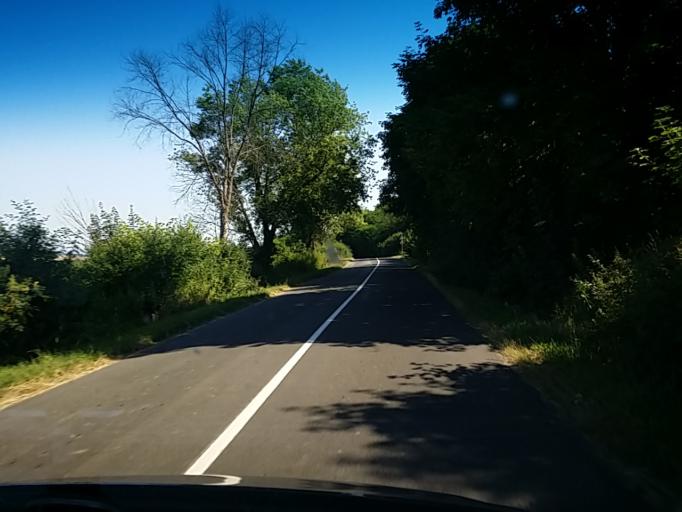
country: HU
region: Nograd
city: Karancskeszi
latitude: 48.2185
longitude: 19.6043
